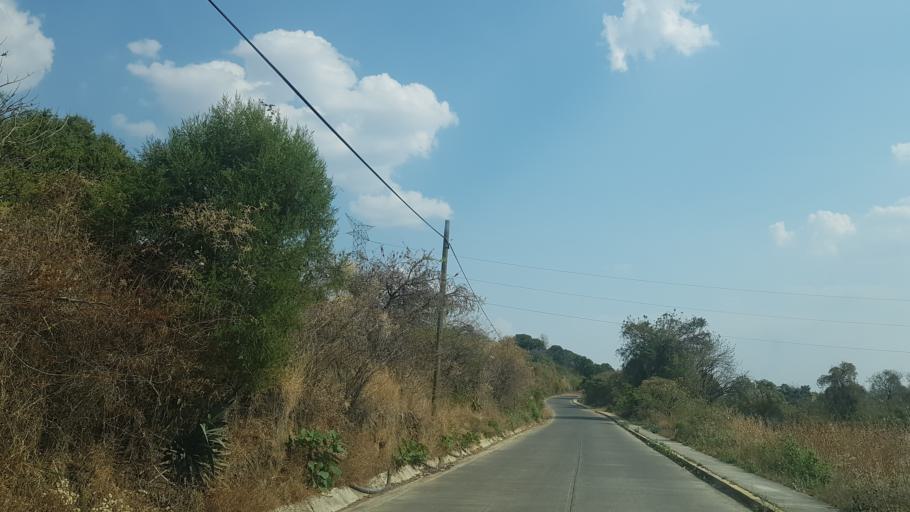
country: MX
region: Puebla
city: San Juan Amecac
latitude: 18.8290
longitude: -98.7040
